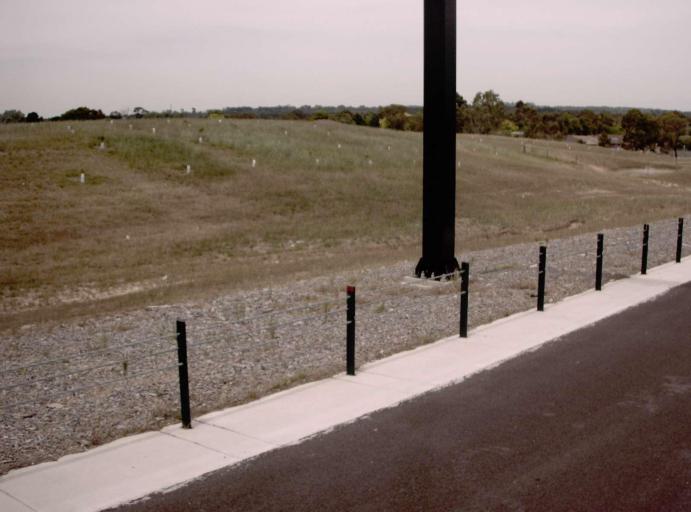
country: AU
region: Victoria
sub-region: Mornington Peninsula
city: Baxter
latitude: -38.1897
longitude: 145.1557
